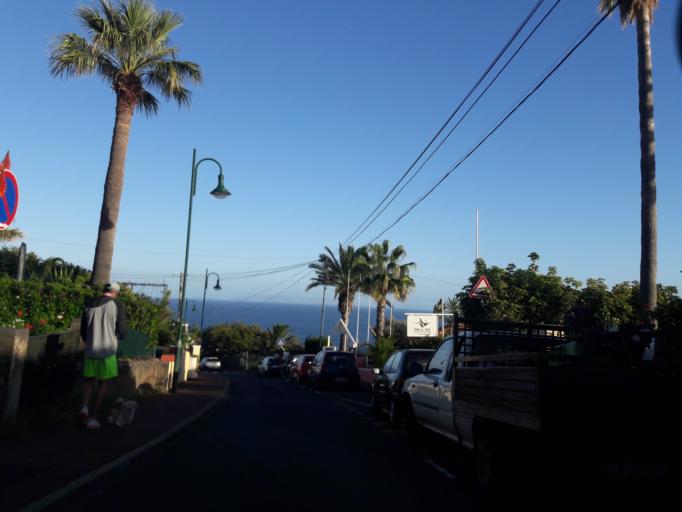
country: PT
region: Madeira
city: Canico
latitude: 32.6418
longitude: -16.8349
